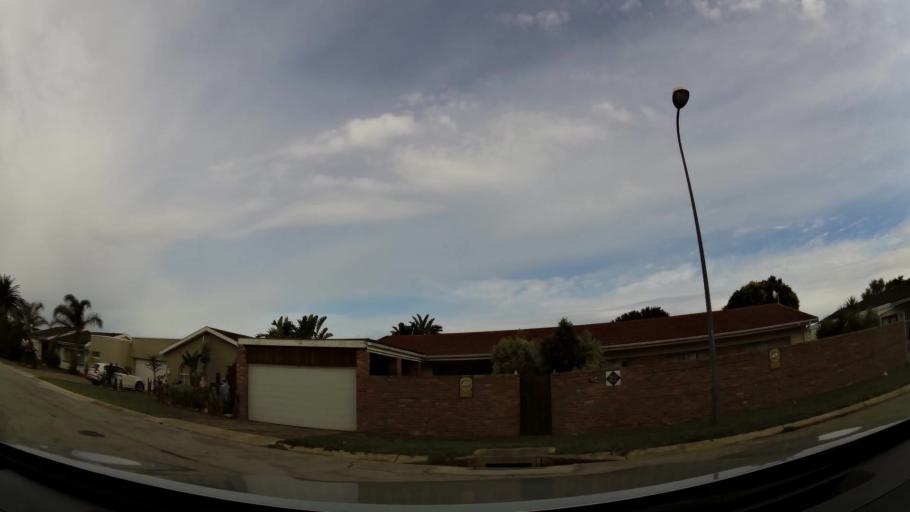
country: ZA
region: Eastern Cape
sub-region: Nelson Mandela Bay Metropolitan Municipality
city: Port Elizabeth
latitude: -33.9354
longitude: 25.4671
